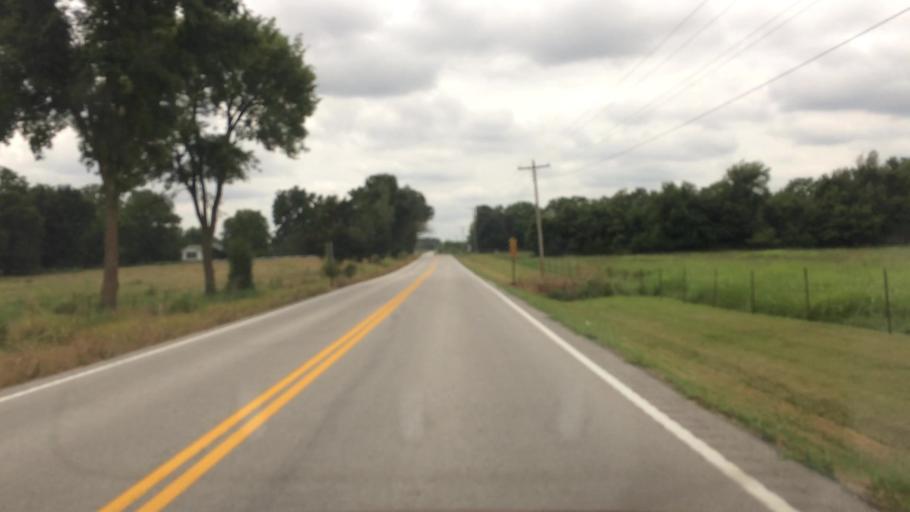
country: US
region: Missouri
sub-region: Greene County
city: Strafford
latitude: 37.2908
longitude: -93.1131
